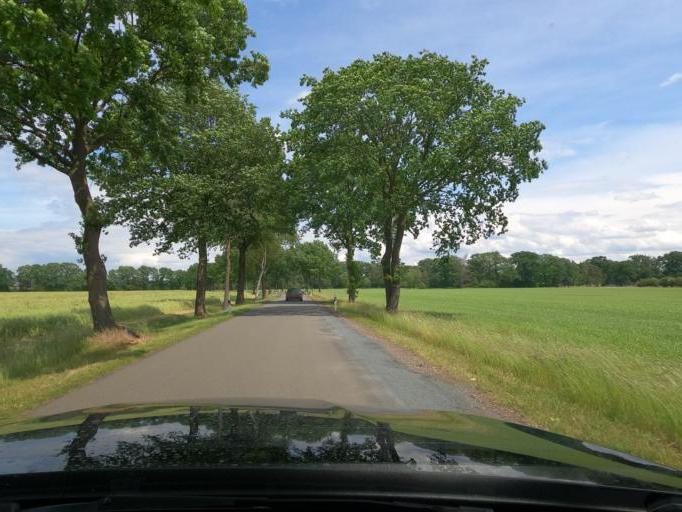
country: DE
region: Lower Saxony
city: Lindwedel
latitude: 52.6181
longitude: 9.6458
